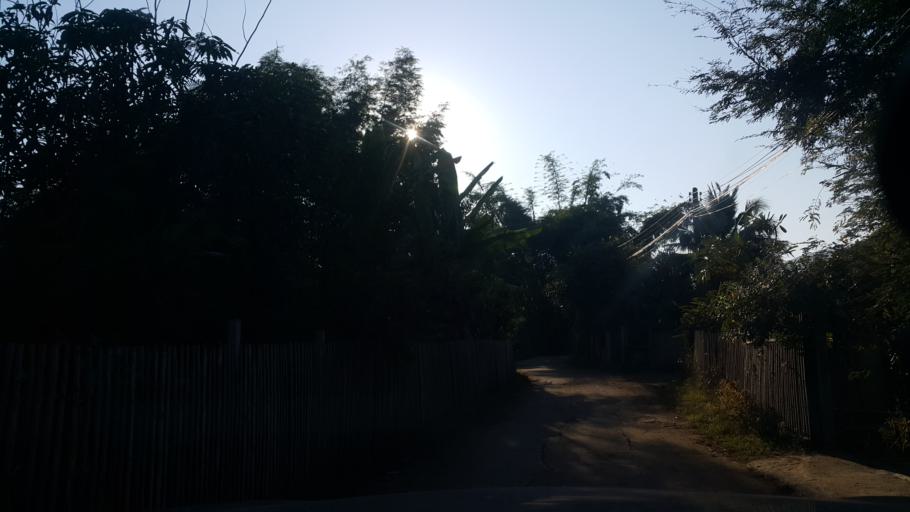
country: TH
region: Chiang Mai
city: Mae On
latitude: 18.7655
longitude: 99.2626
